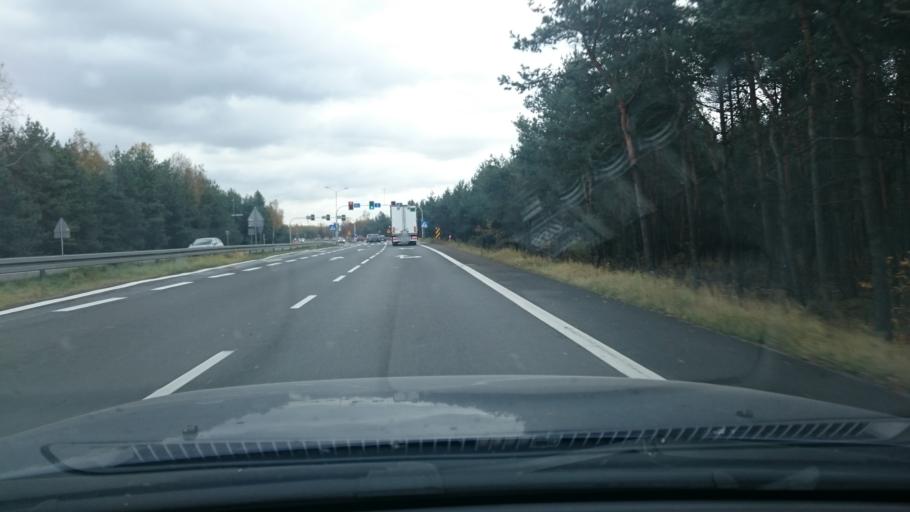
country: PL
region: Lesser Poland Voivodeship
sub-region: Powiat olkuski
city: Boleslaw
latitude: 50.2955
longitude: 19.4982
